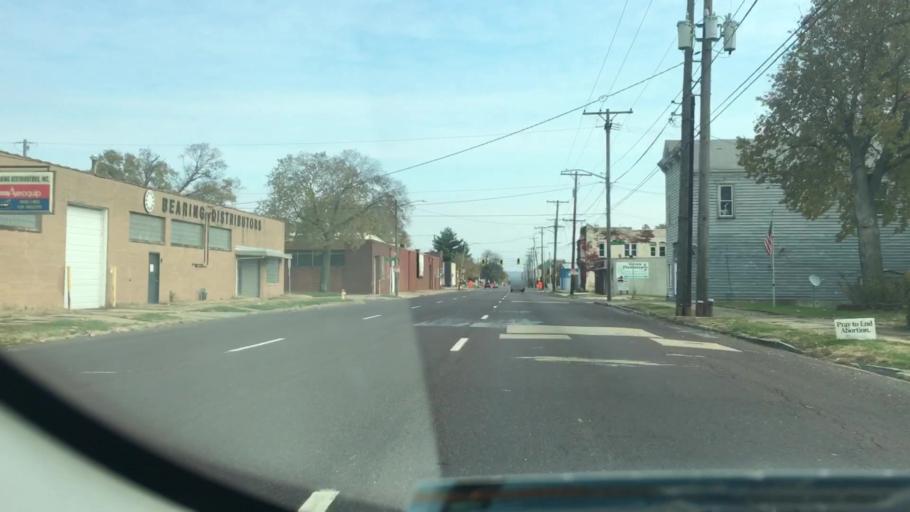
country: US
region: Illinois
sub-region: Peoria County
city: Peoria
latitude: 40.7000
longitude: -89.5768
